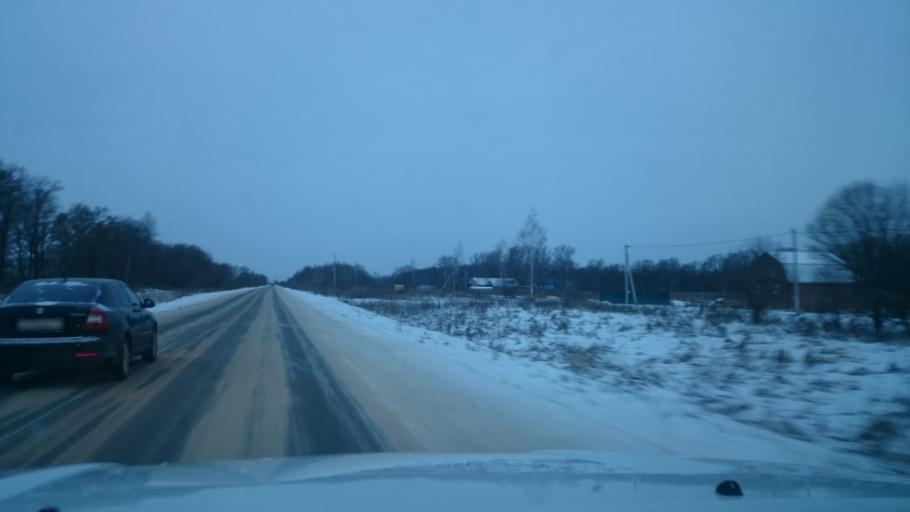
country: RU
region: Tula
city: Leninskiy
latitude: 54.2476
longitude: 37.3907
